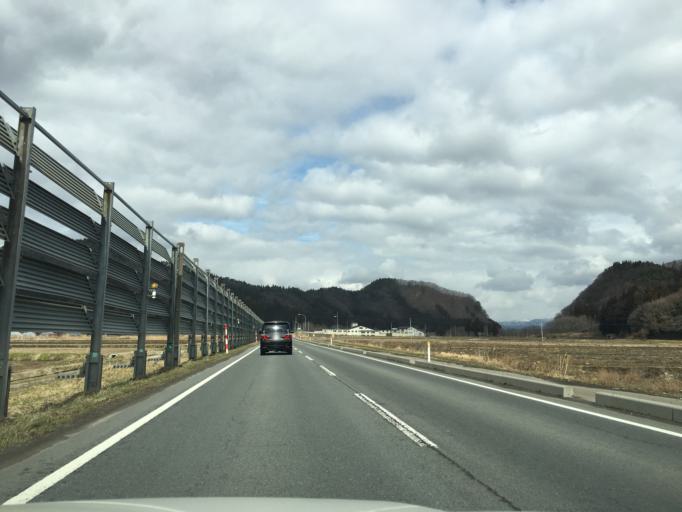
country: JP
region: Akita
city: Hanawa
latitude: 40.2386
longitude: 140.7374
